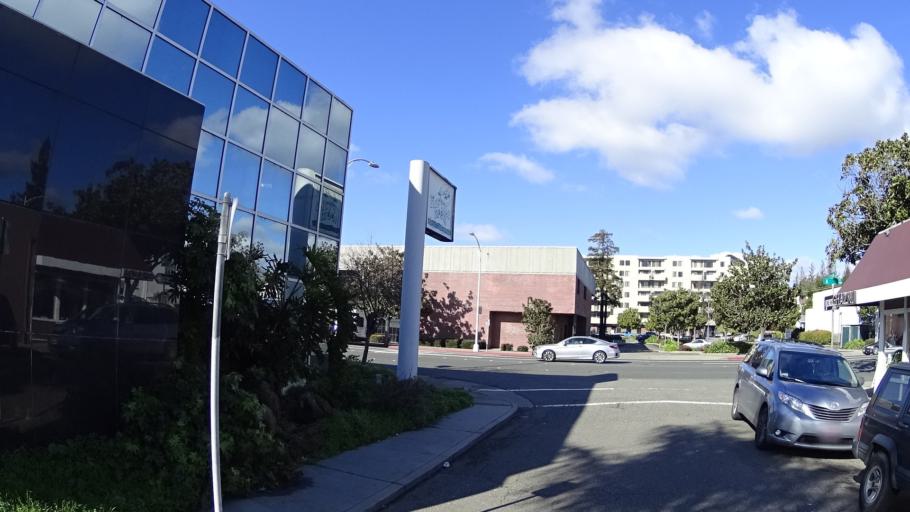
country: US
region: California
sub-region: Alameda County
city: Hayward
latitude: 37.6766
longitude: -122.0796
